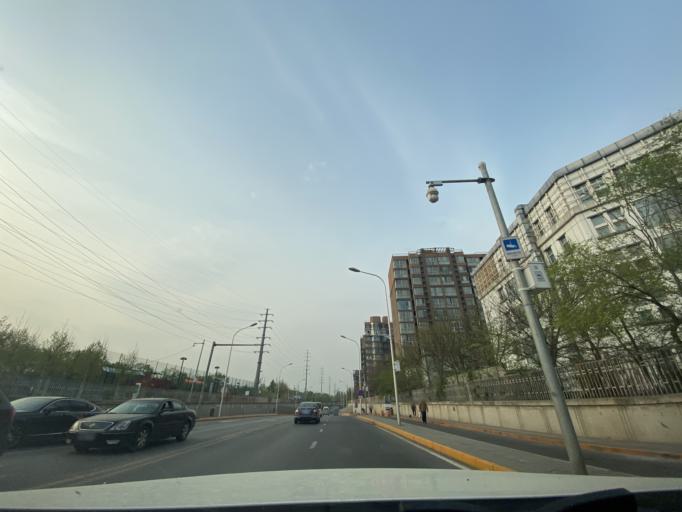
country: CN
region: Beijing
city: Babaoshan
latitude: 39.9286
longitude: 116.2330
